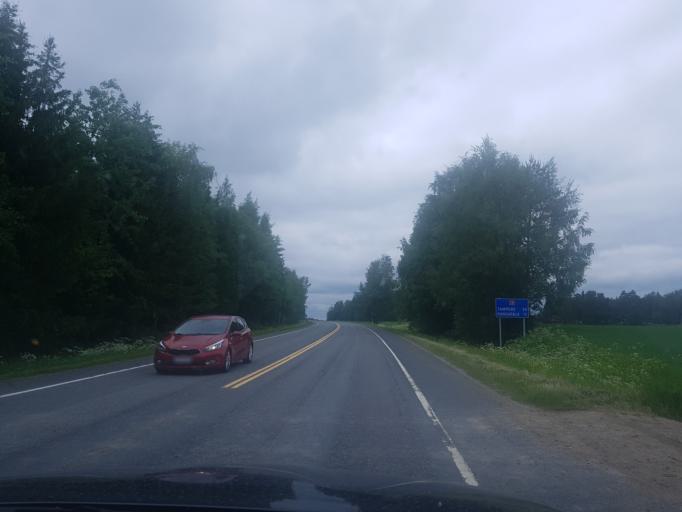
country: FI
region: Pirkanmaa
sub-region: Tampere
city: Paelkaene
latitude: 61.3836
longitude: 24.2410
